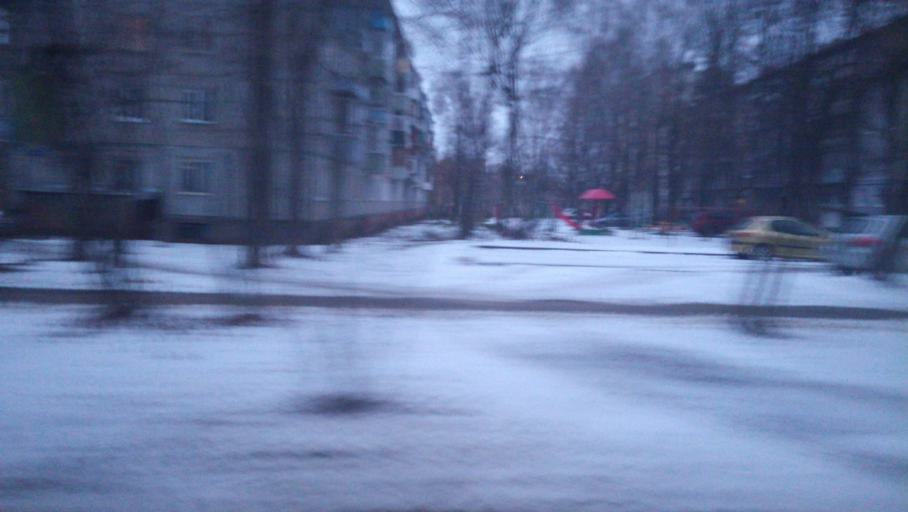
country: RU
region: Tula
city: Kosaya Gora
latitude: 54.1970
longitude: 37.5361
